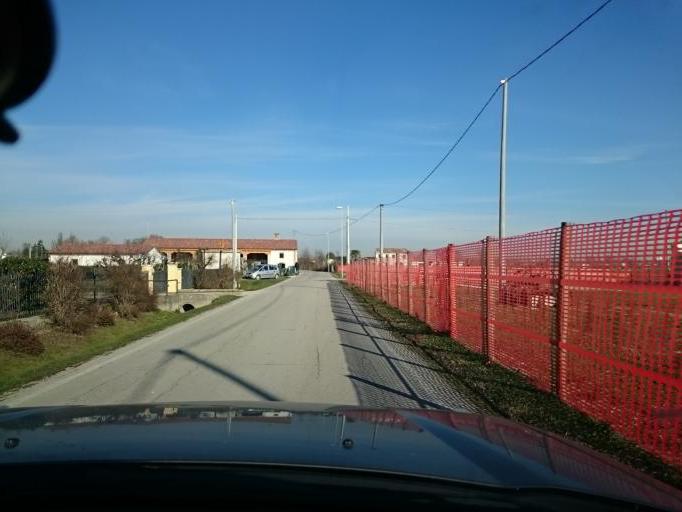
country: IT
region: Veneto
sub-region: Provincia di Venezia
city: Mira Taglio
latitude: 45.4225
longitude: 12.1117
